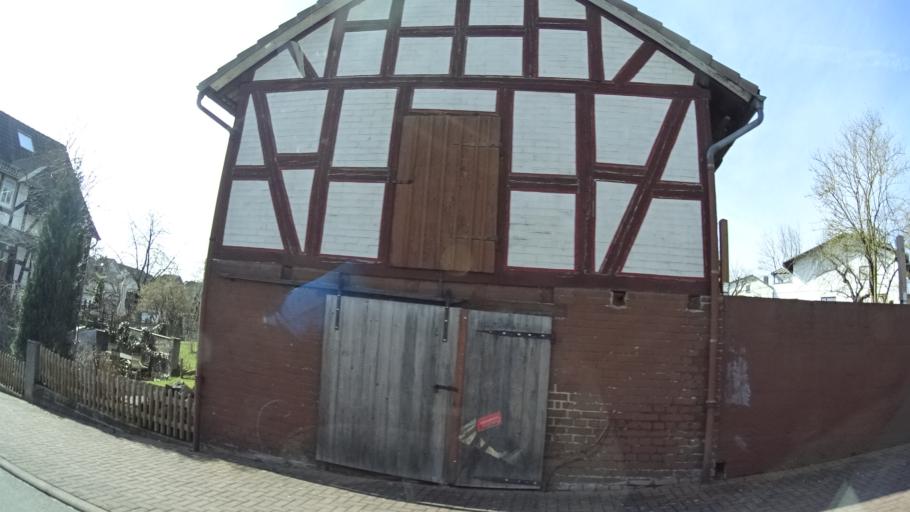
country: DE
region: Hesse
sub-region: Regierungsbezirk Giessen
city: Grunberg
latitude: 50.6194
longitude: 8.9332
